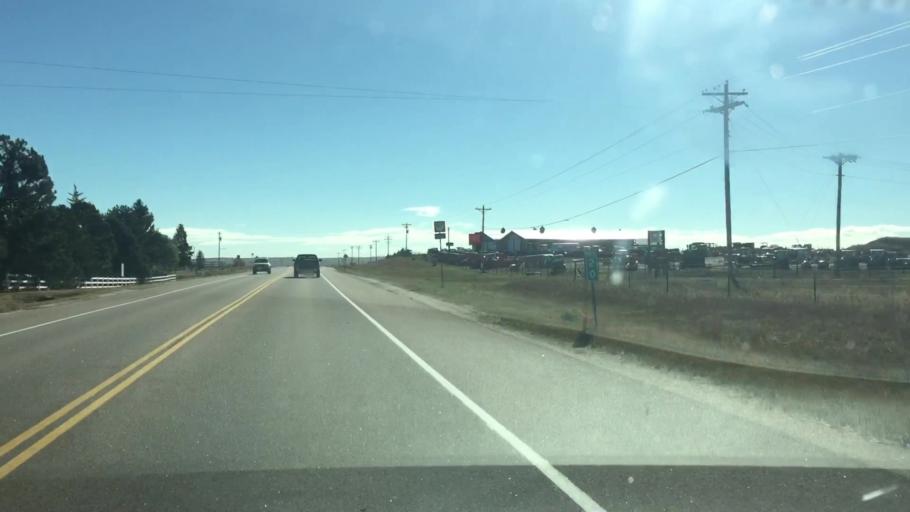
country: US
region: Colorado
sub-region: Elbert County
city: Kiowa
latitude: 39.3557
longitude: -104.5201
